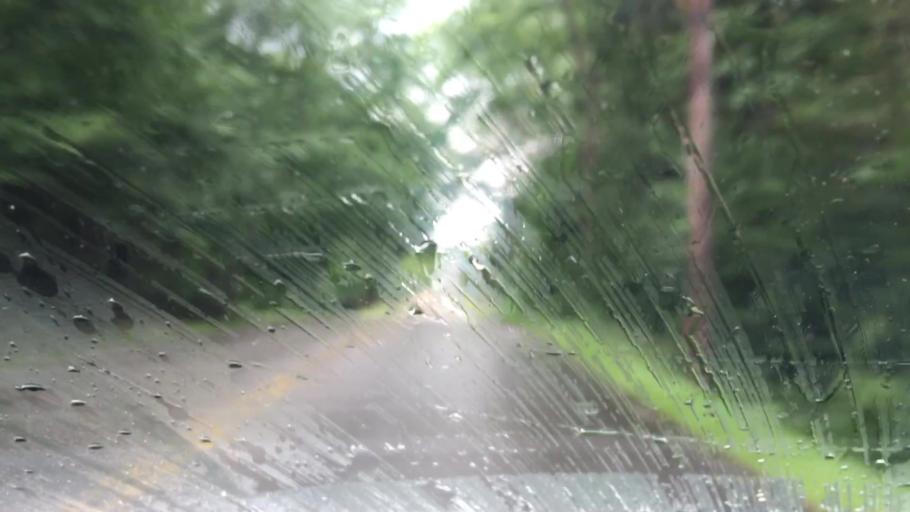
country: US
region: Maine
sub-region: York County
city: Wells Beach Station
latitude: 43.2963
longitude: -70.6028
